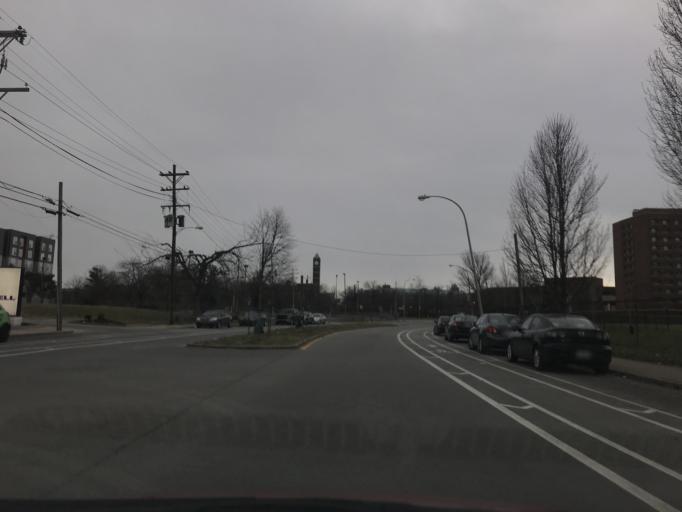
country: US
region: Kentucky
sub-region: Jefferson County
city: Louisville
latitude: 38.2215
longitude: -85.7561
